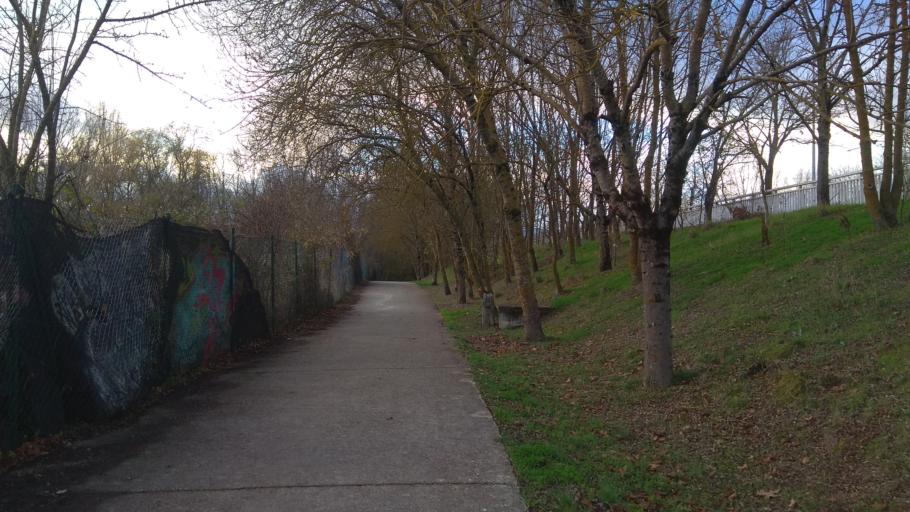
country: ES
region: Navarre
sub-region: Provincia de Navarra
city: Baranain
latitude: 42.8084
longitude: -1.6802
